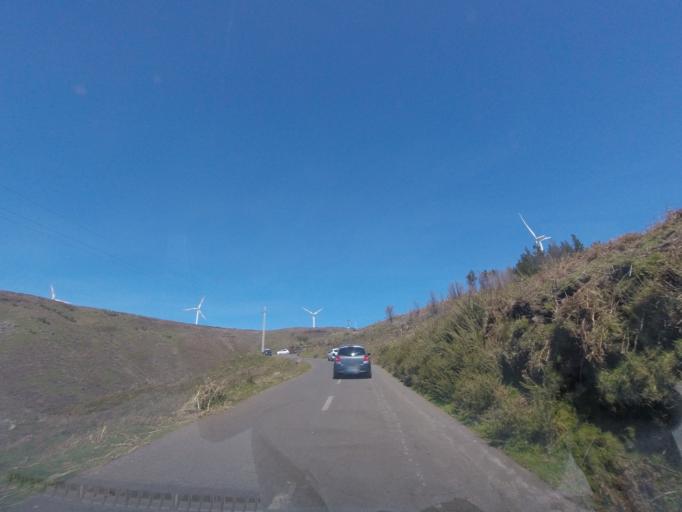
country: PT
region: Madeira
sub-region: Calheta
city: Arco da Calheta
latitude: 32.7400
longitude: -17.1024
